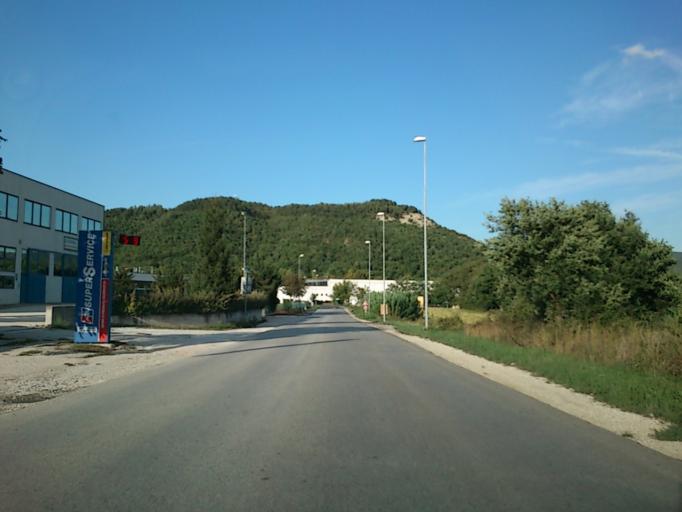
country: IT
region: The Marches
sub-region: Provincia di Pesaro e Urbino
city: Fermignano
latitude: 43.6942
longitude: 12.6602
